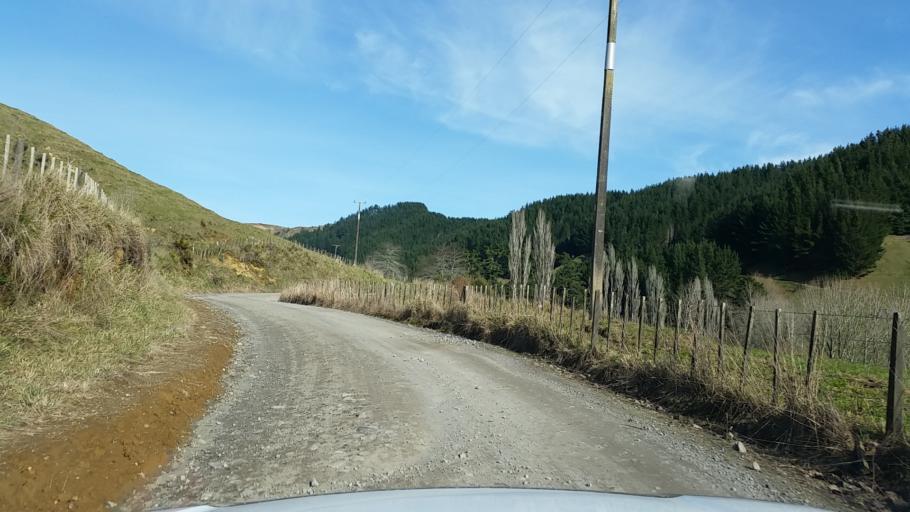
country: NZ
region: Taranaki
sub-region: South Taranaki District
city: Eltham
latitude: -39.3552
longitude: 174.5132
